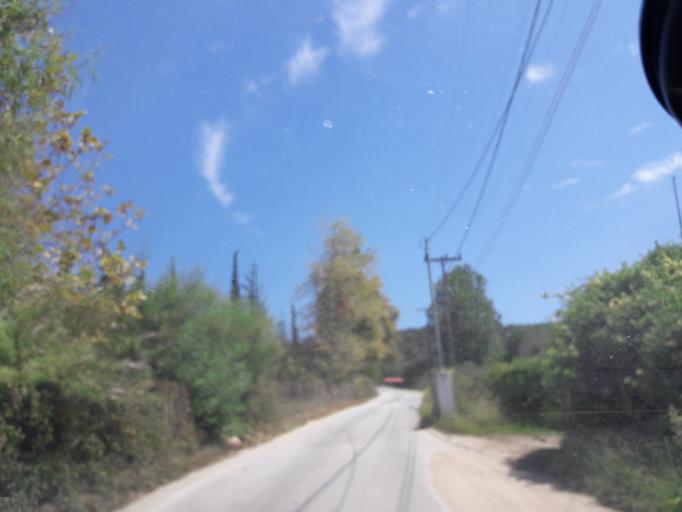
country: GR
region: Central Macedonia
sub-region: Nomos Chalkidikis
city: Ouranoupolis
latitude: 40.3158
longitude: 23.9285
